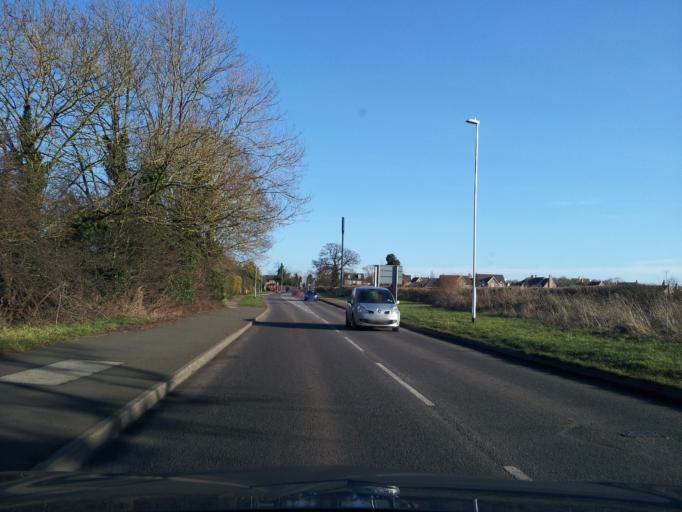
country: GB
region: England
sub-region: Northamptonshire
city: Bugbrooke
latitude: 52.2504
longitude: -0.9677
